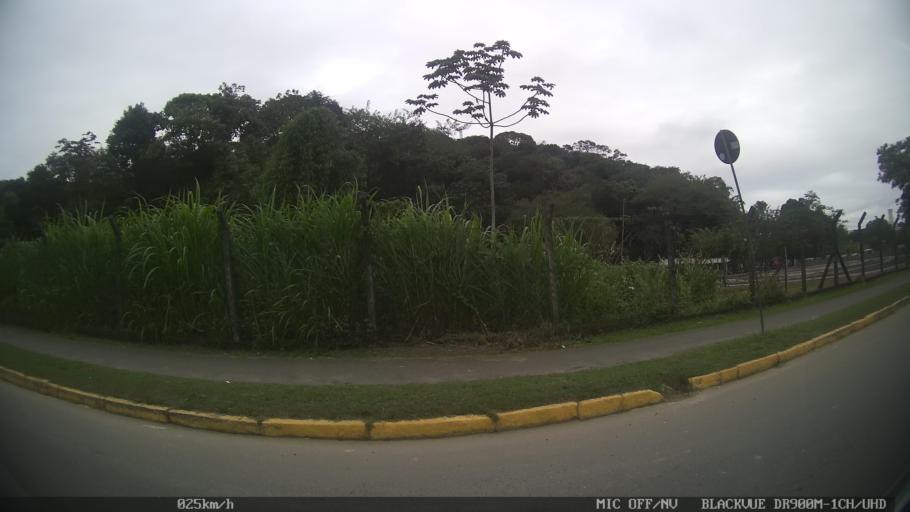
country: BR
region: Santa Catarina
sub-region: Joinville
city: Joinville
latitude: -26.2962
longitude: -48.8813
